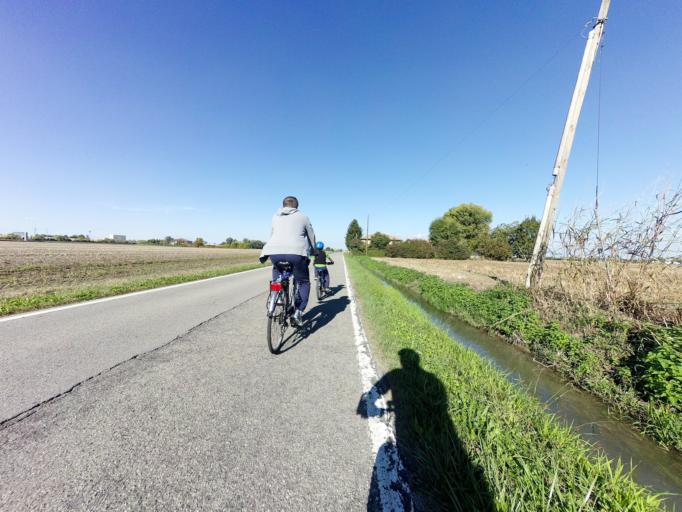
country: IT
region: Emilia-Romagna
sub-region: Provincia di Bologna
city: Progresso
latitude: 44.5760
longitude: 11.3948
